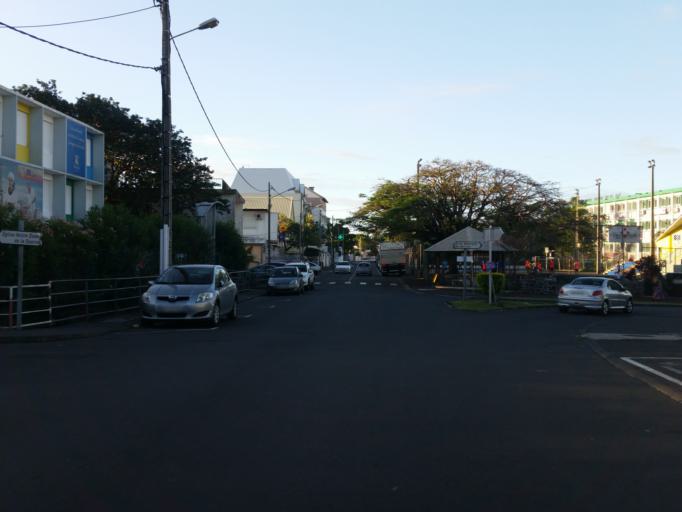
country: RE
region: Reunion
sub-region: Reunion
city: Saint-Denis
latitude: -20.8909
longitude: 55.4479
